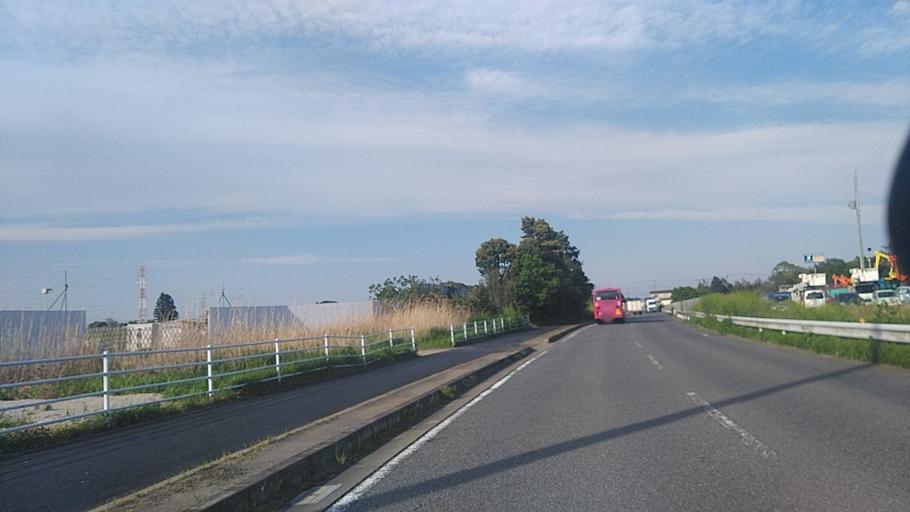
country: JP
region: Chiba
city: Shiroi
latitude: 35.7698
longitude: 140.1091
